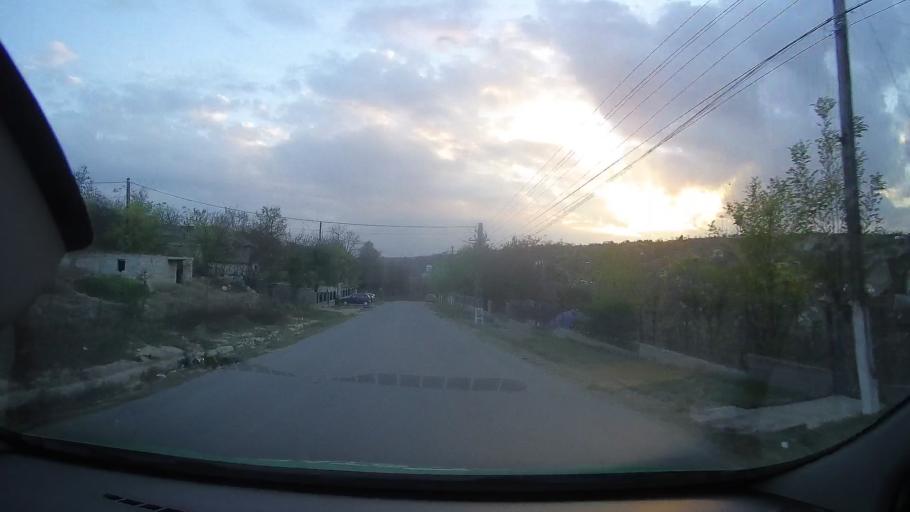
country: RO
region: Constanta
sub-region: Comuna Lipnita
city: Lipnita
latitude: 44.0955
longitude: 27.6080
